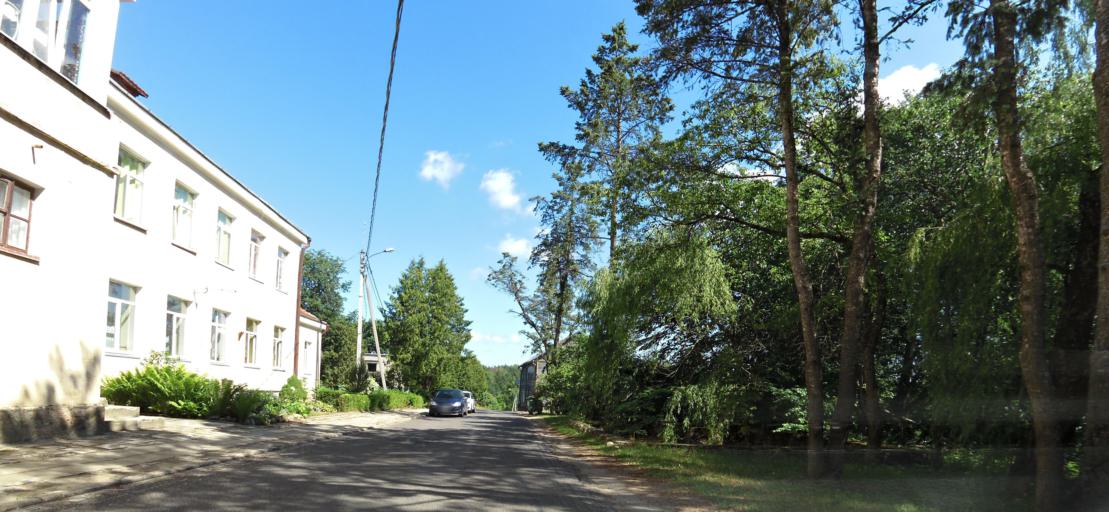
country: LT
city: Nemencine
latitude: 54.7947
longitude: 25.3976
